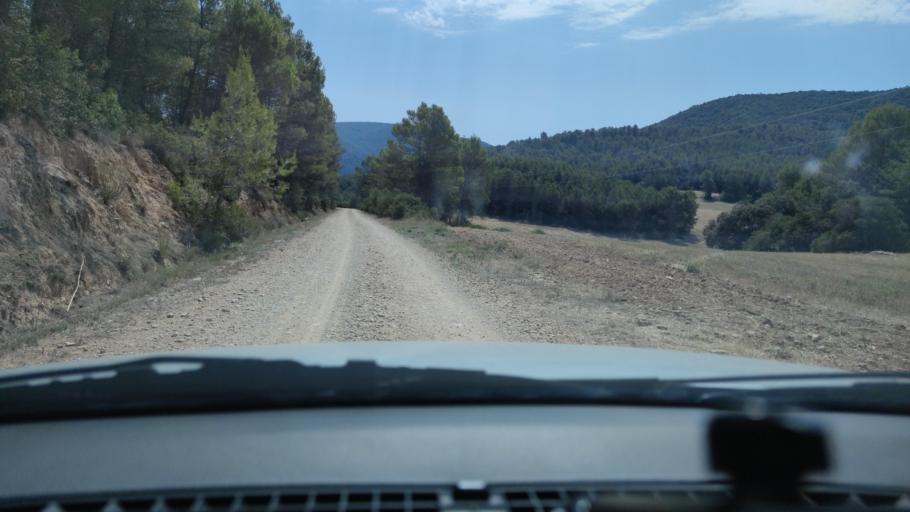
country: ES
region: Catalonia
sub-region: Provincia de Lleida
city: Camarasa
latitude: 41.9250
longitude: 0.8417
